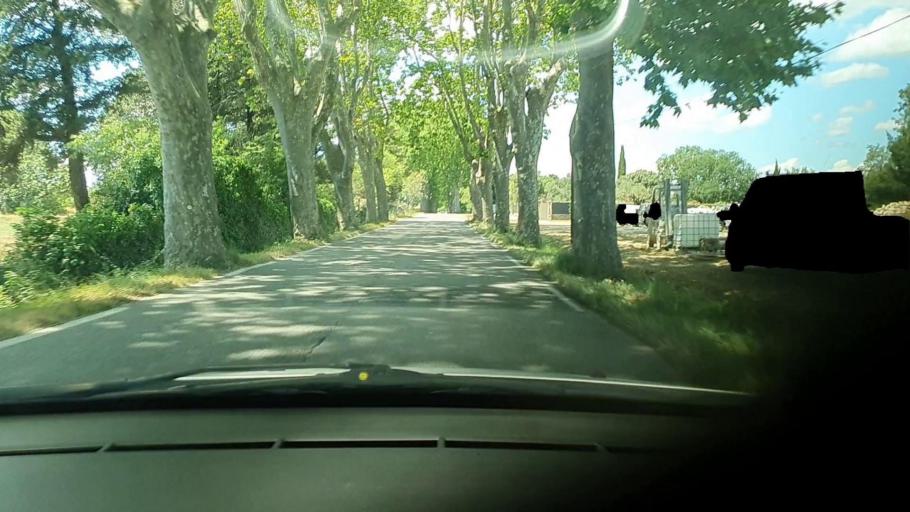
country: FR
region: Languedoc-Roussillon
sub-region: Departement du Gard
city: Montaren-et-Saint-Mediers
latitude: 44.0225
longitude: 4.3946
